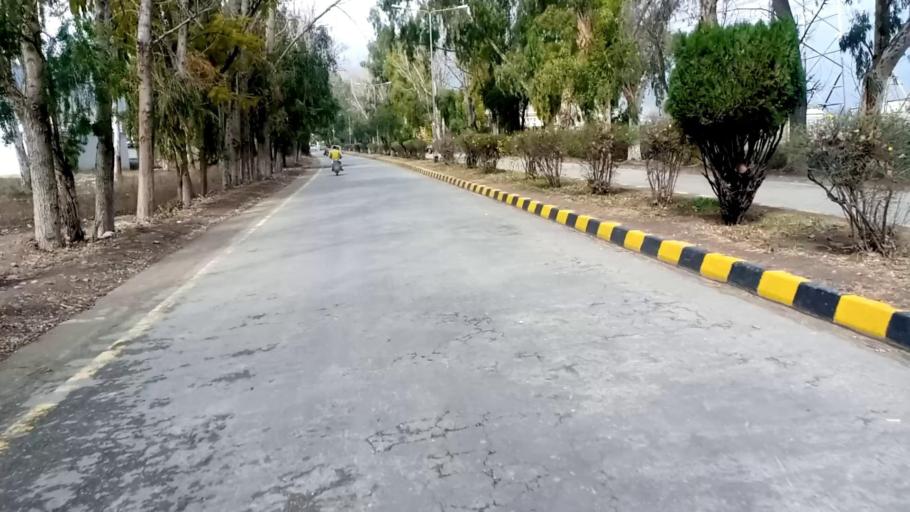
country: PK
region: Khyber Pakhtunkhwa
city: Mingora
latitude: 34.8179
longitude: 72.3411
